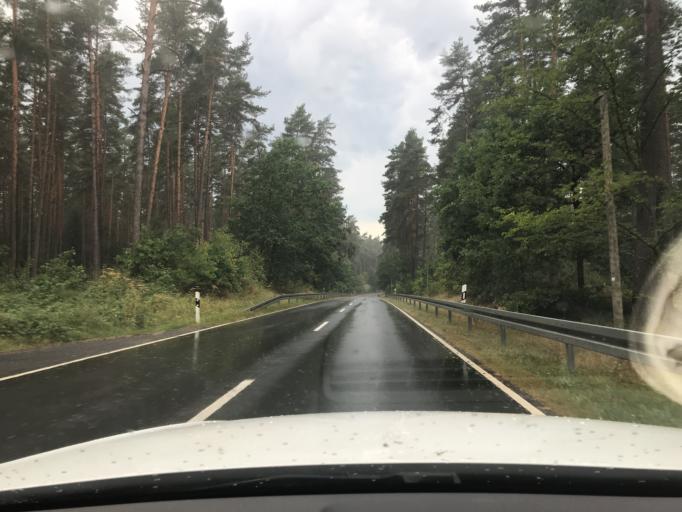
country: DE
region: Bavaria
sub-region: Upper Palatinate
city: Speinshart
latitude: 49.7737
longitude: 11.7861
